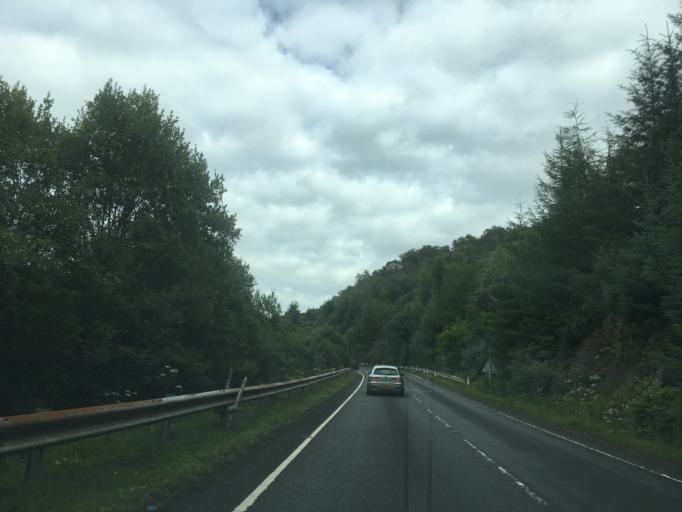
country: GB
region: Scotland
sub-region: Argyll and Bute
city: Oban
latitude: 56.3117
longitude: -5.4770
